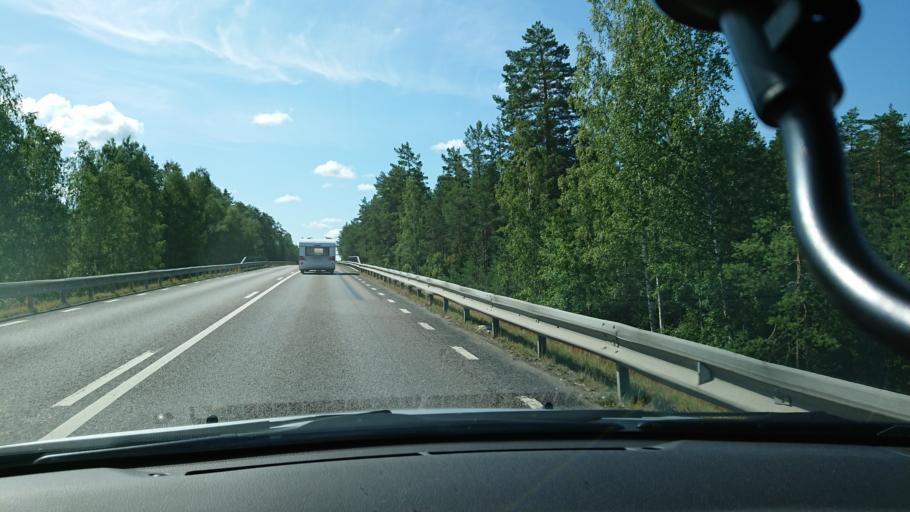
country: SE
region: Kalmar
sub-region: Vimmerby Kommun
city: Sodra Vi
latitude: 57.7514
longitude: 15.7741
